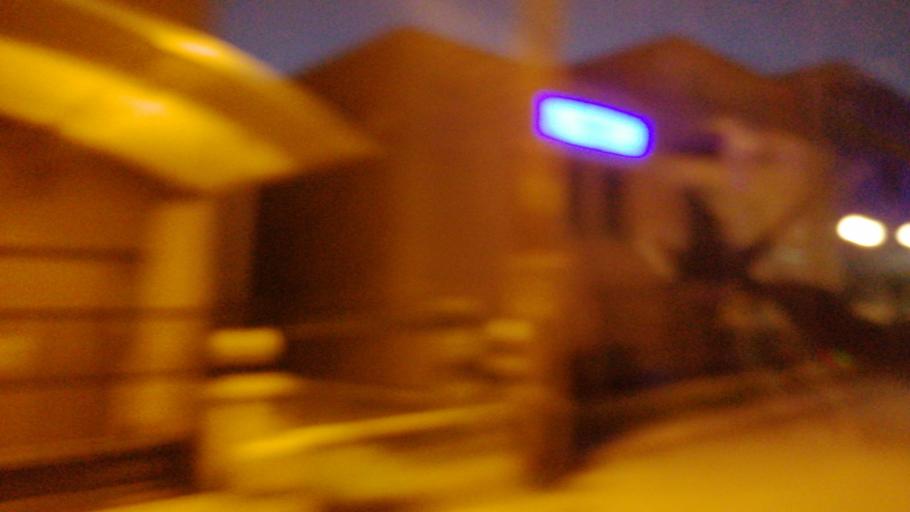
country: TR
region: Istanbul
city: Umraniye
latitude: 40.9969
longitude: 29.1426
